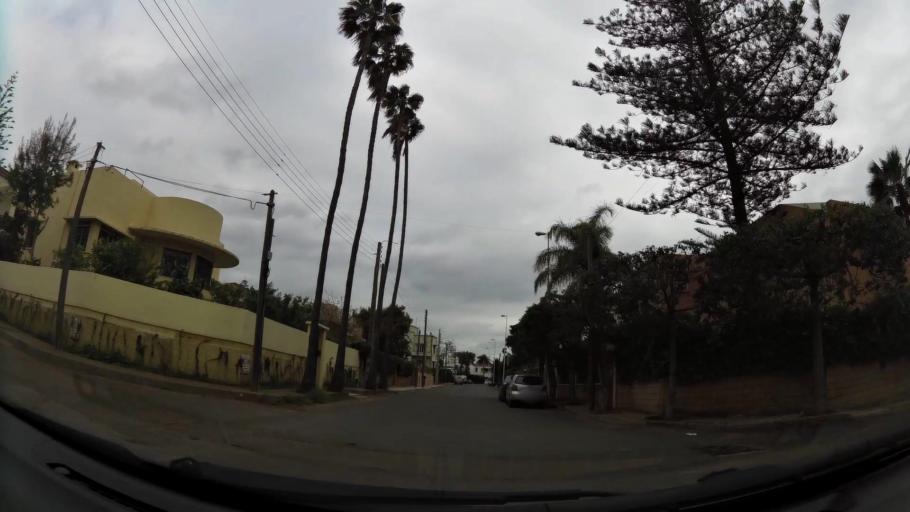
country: MA
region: Grand Casablanca
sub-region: Casablanca
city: Casablanca
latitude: 33.5529
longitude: -7.6384
